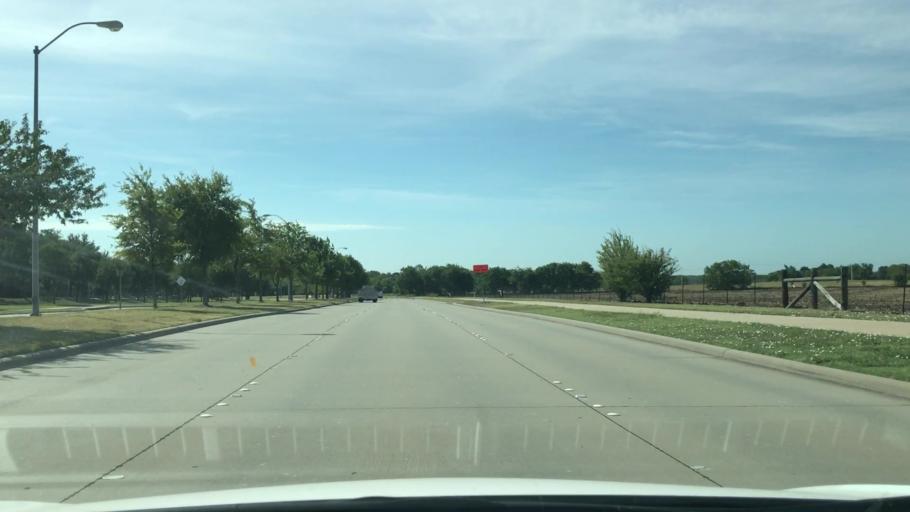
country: US
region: Texas
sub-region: Denton County
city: The Colony
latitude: 33.0606
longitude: -96.8108
